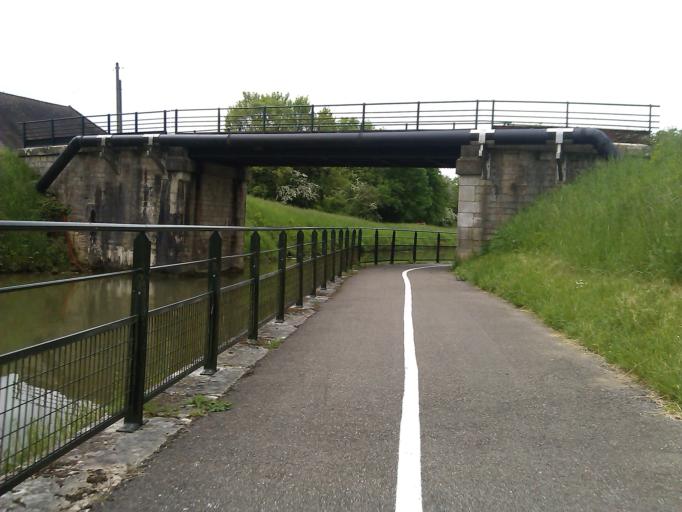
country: FR
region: Franche-Comte
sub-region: Departement du Jura
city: Choisey
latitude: 47.0729
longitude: 5.4703
